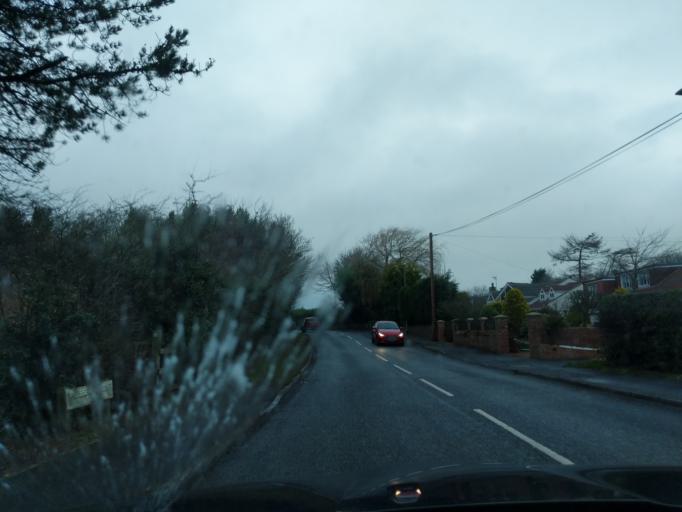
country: GB
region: England
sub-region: Northumberland
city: Bedlington
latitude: 55.1160
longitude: -1.6245
